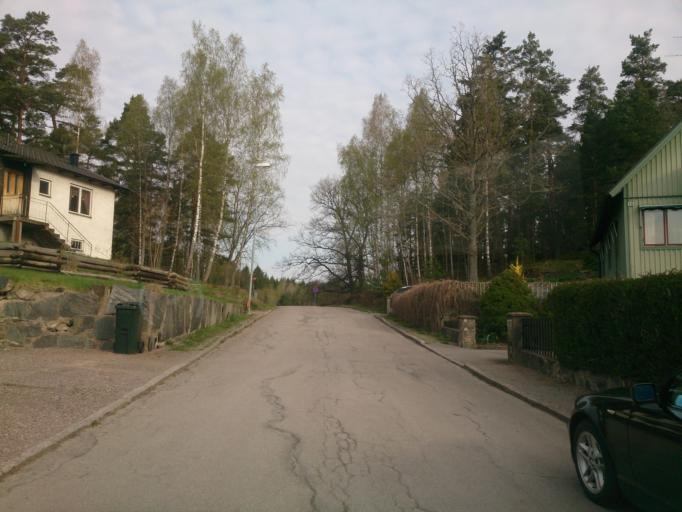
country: SE
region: OEstergoetland
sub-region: Atvidabergs Kommun
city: Atvidaberg
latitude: 58.2118
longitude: 16.0086
